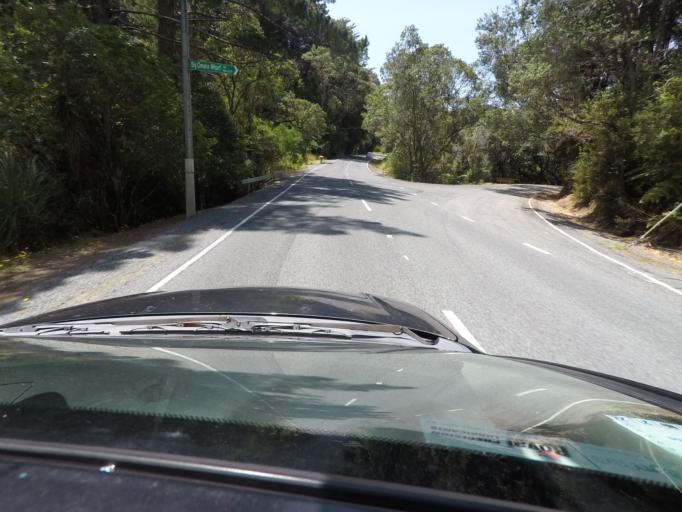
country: NZ
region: Auckland
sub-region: Auckland
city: Warkworth
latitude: -36.3152
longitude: 174.7545
